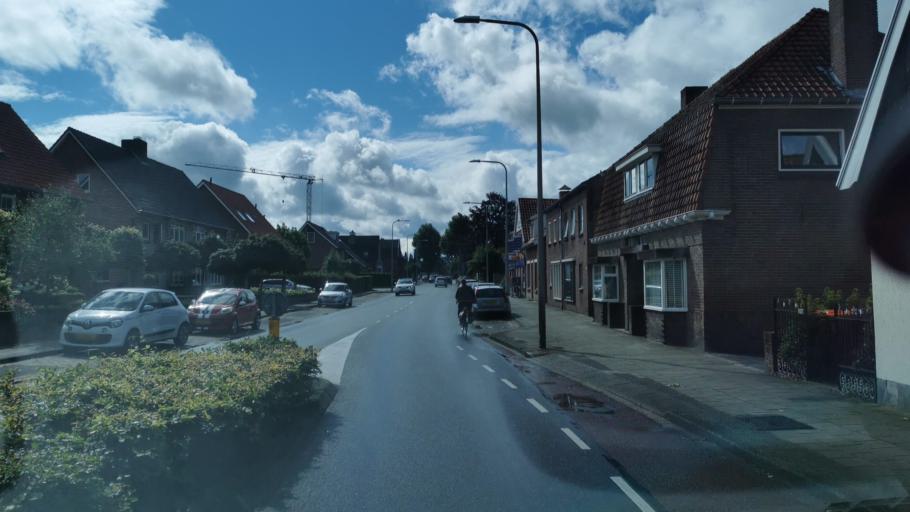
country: NL
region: Overijssel
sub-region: Gemeente Haaksbergen
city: Haaksbergen
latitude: 52.1598
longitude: 6.7338
